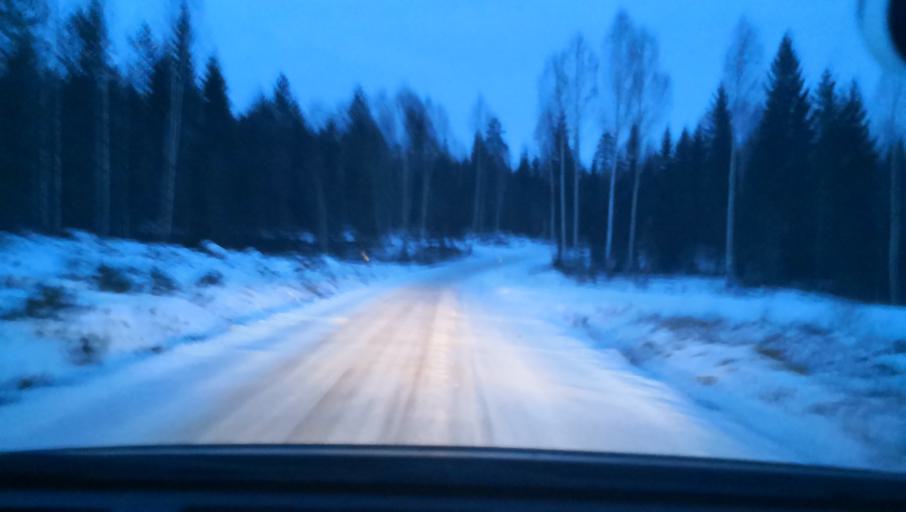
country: SE
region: Dalarna
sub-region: Avesta Kommun
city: Horndal
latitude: 60.2302
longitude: 16.6473
